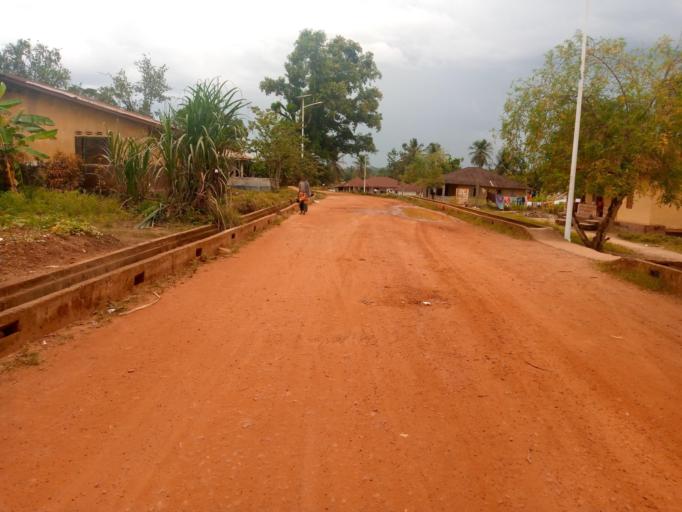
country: SL
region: Southern Province
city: Mogbwemo
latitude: 7.6068
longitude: -12.1742
